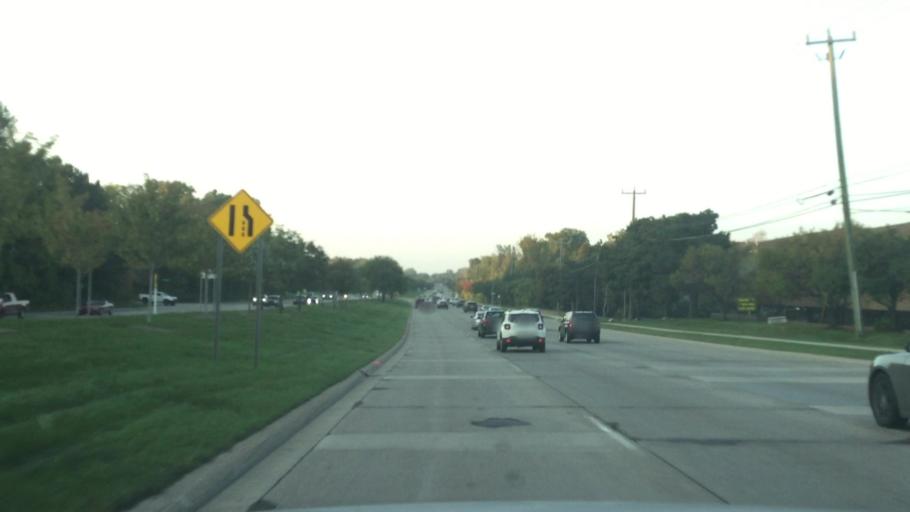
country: US
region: Michigan
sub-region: Oakland County
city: Bloomfield Hills
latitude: 42.5835
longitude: -83.2809
